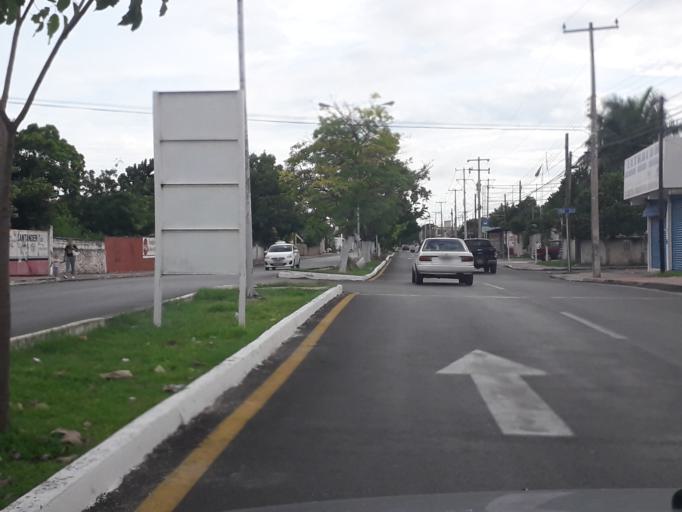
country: MX
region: Yucatan
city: Merida
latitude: 20.9700
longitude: -89.6636
